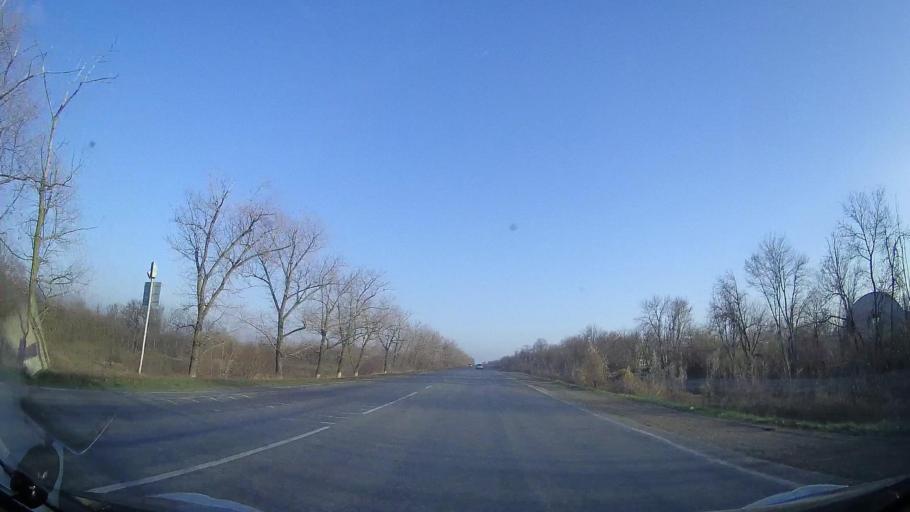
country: RU
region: Rostov
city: Bataysk
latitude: 47.0726
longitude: 39.7918
